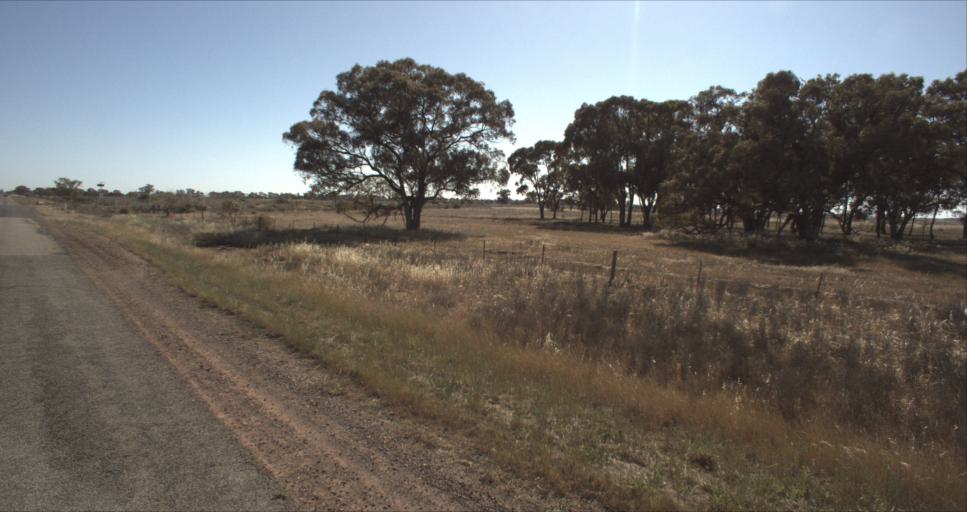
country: AU
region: New South Wales
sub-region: Leeton
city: Leeton
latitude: -34.5891
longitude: 146.2600
